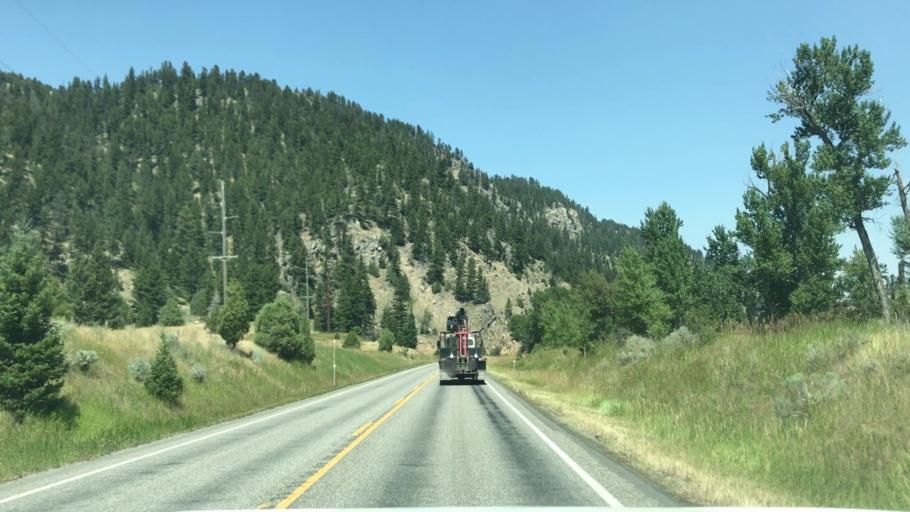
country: US
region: Montana
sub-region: Gallatin County
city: Four Corners
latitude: 45.4983
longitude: -111.2711
